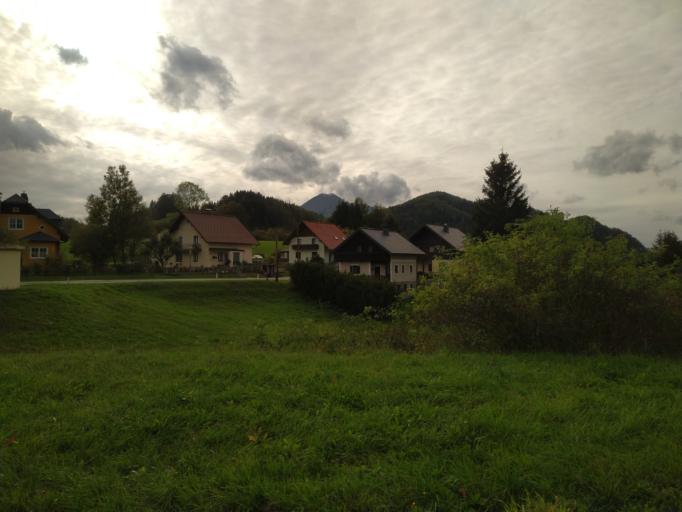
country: AT
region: Lower Austria
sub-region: Politischer Bezirk Lilienfeld
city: Mitterbach am Erlaufsee
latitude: 47.8649
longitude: 15.3108
